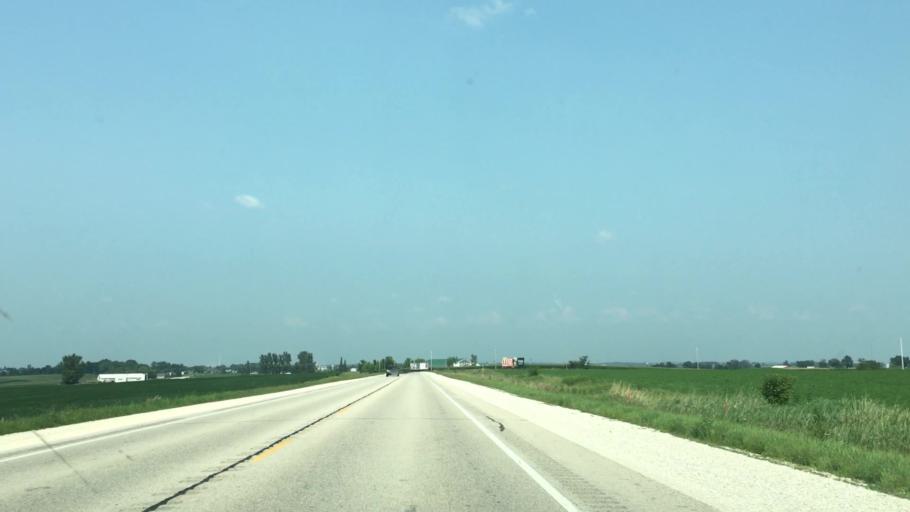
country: US
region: Iowa
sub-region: Winneshiek County
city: Decorah
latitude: 43.2507
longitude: -91.8411
